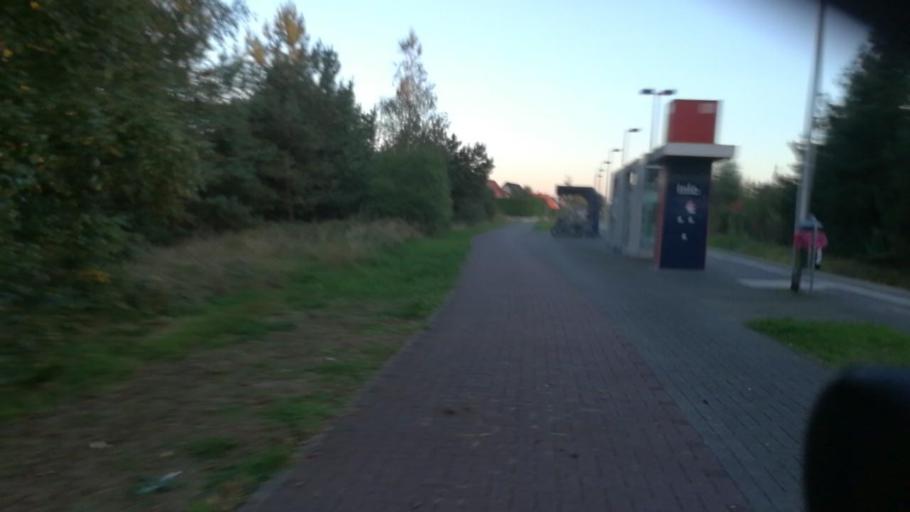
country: DE
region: North Rhine-Westphalia
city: Halle
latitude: 52.0368
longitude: 8.3841
